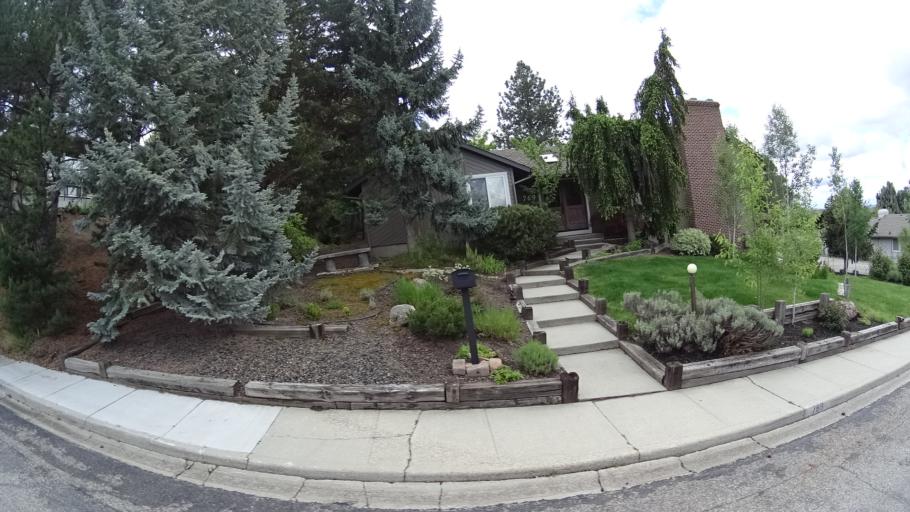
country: US
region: Idaho
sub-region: Ada County
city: Boise
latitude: 43.6520
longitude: -116.1803
